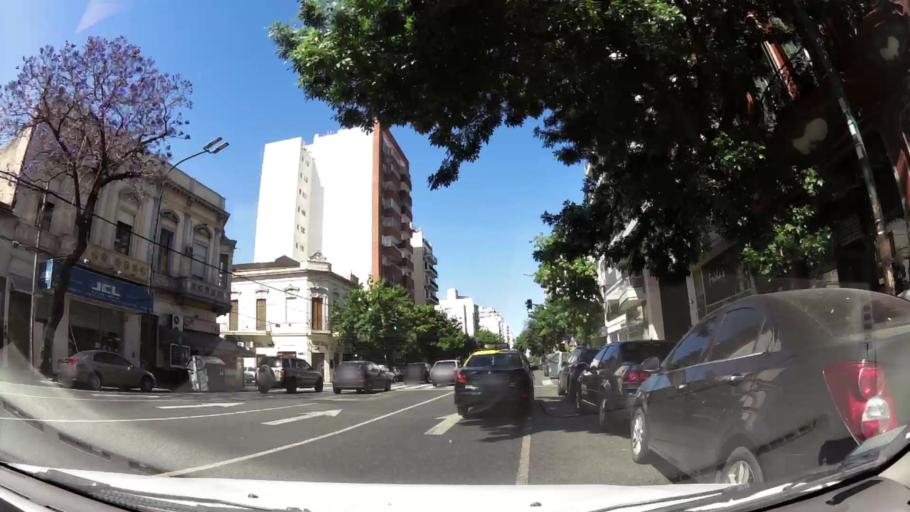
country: AR
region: Buenos Aires F.D.
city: Buenos Aires
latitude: -34.6241
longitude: -58.4043
